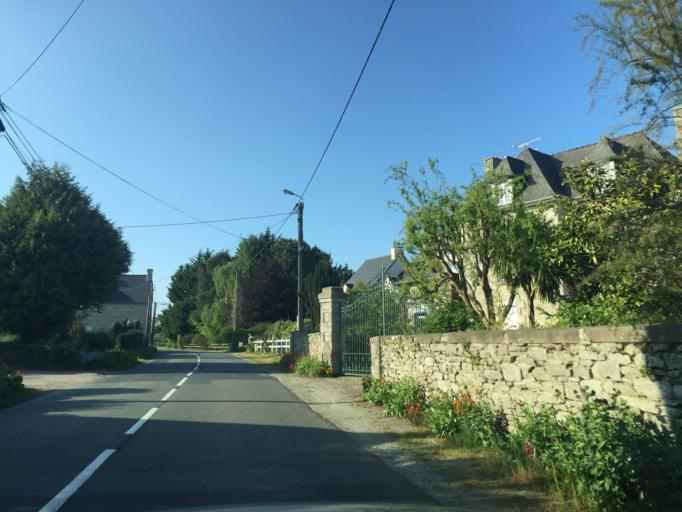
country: FR
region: Brittany
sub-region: Departement des Cotes-d'Armor
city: Saint-Cast-le-Guildo
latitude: 48.6148
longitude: -2.2541
